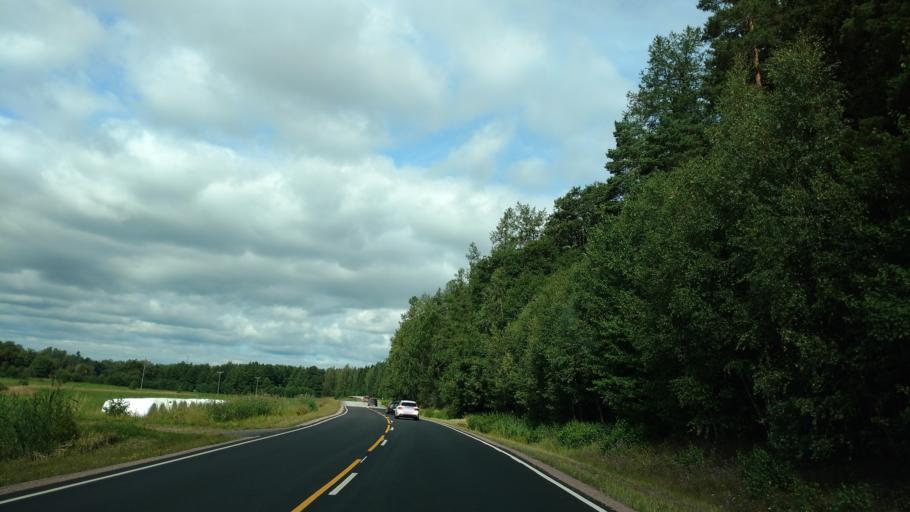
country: FI
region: Varsinais-Suomi
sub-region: Salo
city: Saerkisalo
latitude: 60.1853
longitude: 22.8942
